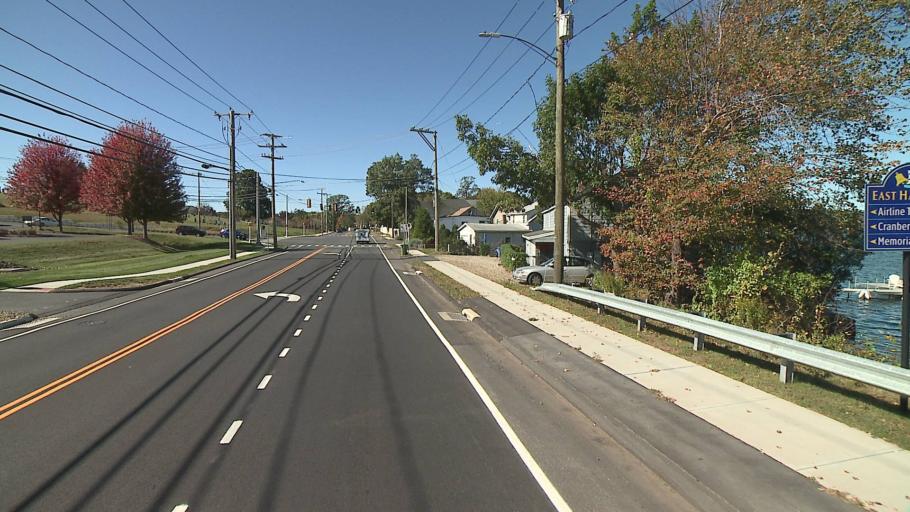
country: US
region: Connecticut
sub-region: Middlesex County
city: East Hampton
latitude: 41.5849
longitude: -72.4975
